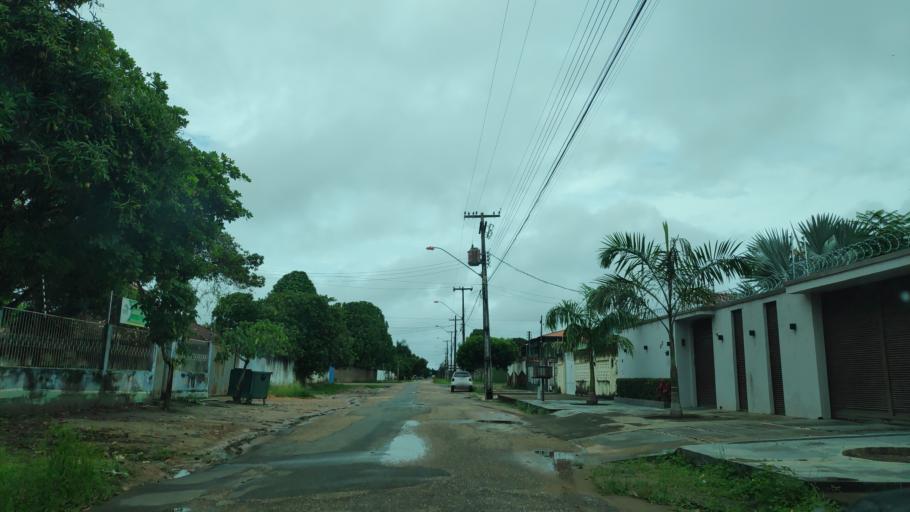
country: BR
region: Roraima
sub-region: Boa Vista
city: Boa Vista
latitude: 2.8342
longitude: -60.7016
